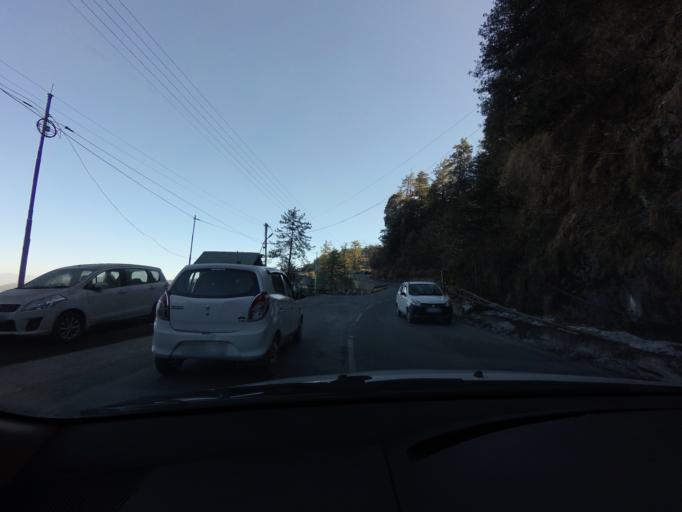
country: IN
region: Himachal Pradesh
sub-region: Shimla
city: Shimla
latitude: 31.1097
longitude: 77.2162
